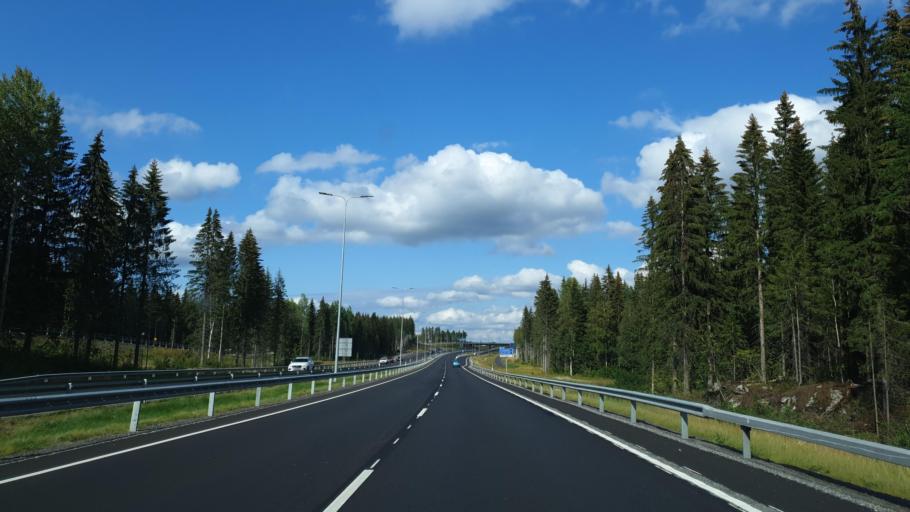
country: FI
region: Southern Savonia
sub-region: Mikkeli
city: Mikkeli
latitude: 61.7067
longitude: 27.3287
